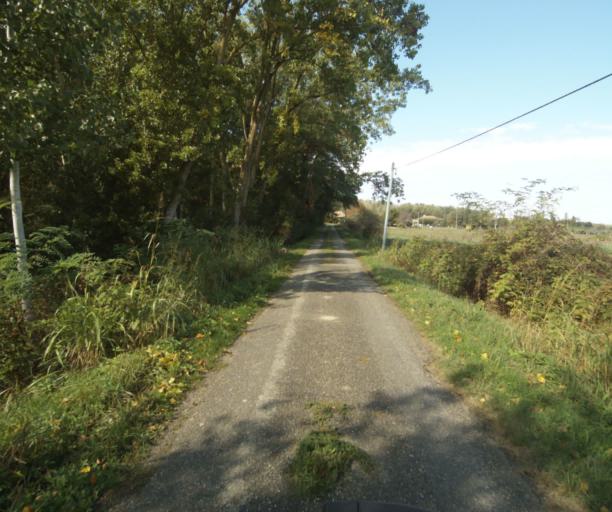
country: FR
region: Midi-Pyrenees
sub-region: Departement du Tarn-et-Garonne
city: Verdun-sur-Garonne
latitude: 43.8788
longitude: 1.2258
